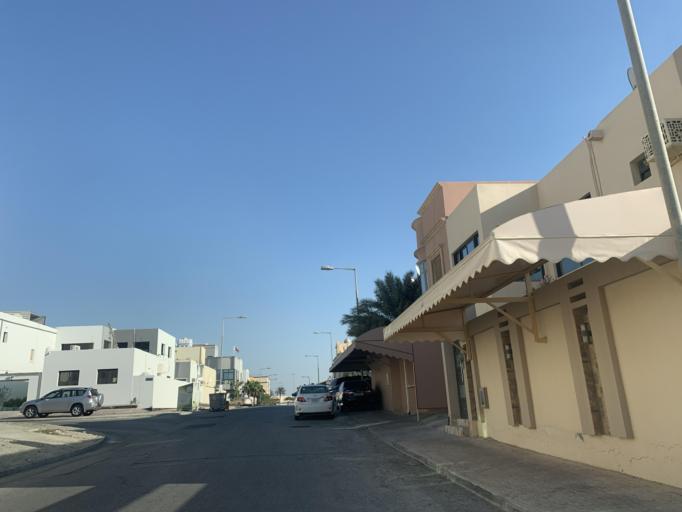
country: BH
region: Central Governorate
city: Madinat Hamad
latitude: 26.1091
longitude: 50.5084
